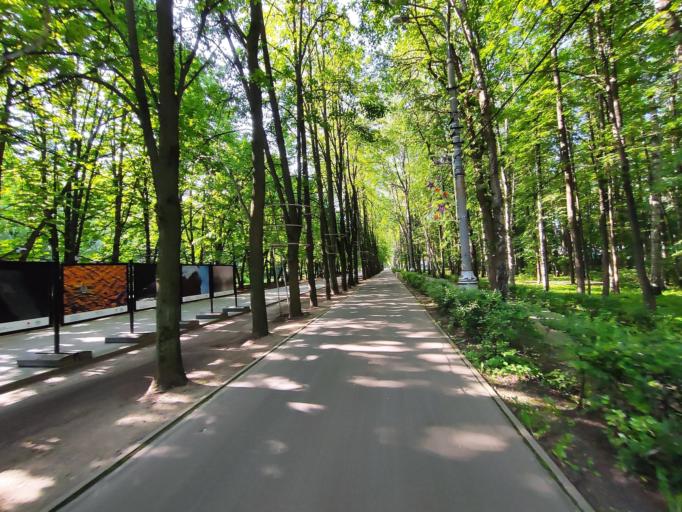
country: RU
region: Moscow
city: Metrogorodok
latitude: 55.7841
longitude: 37.7512
